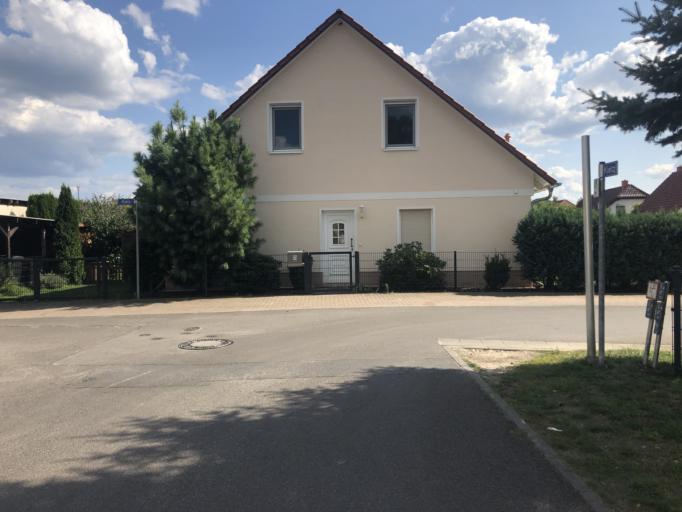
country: DE
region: Brandenburg
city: Mullrose
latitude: 52.2484
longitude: 14.4116
